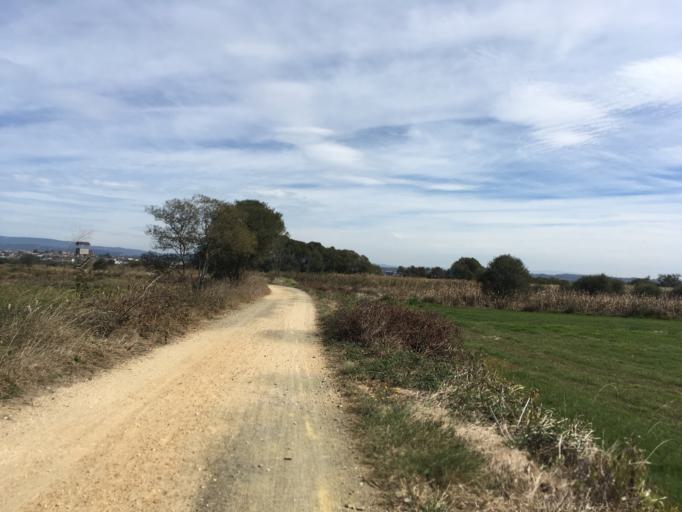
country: PT
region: Aveiro
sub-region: Estarreja
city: Estarreja
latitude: 40.7309
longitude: -8.5936
